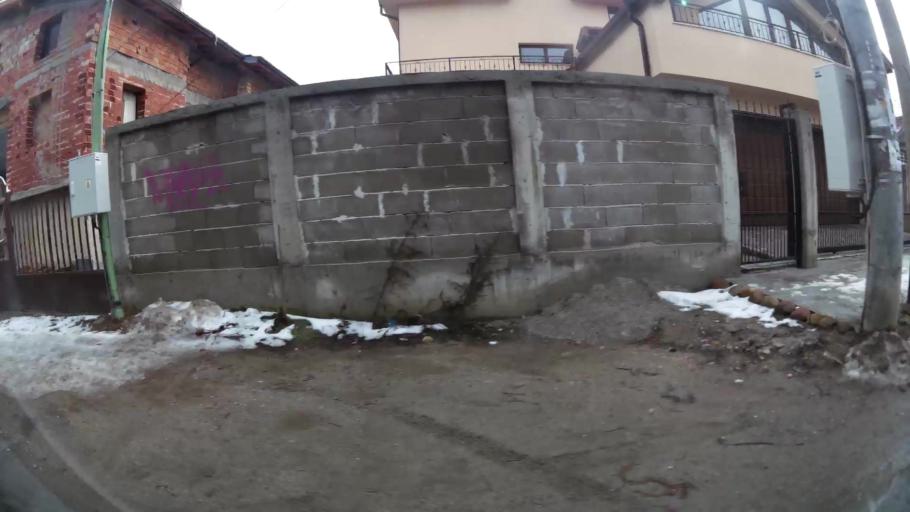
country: BG
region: Sofia-Capital
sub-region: Stolichna Obshtina
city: Sofia
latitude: 42.6607
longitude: 23.2401
